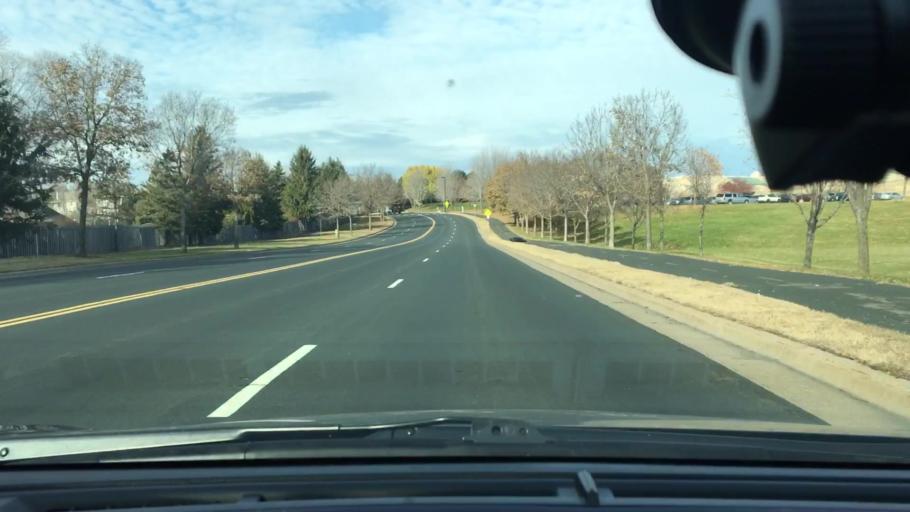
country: US
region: Minnesota
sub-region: Hennepin County
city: Maple Grove
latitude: 45.1081
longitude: -93.4832
